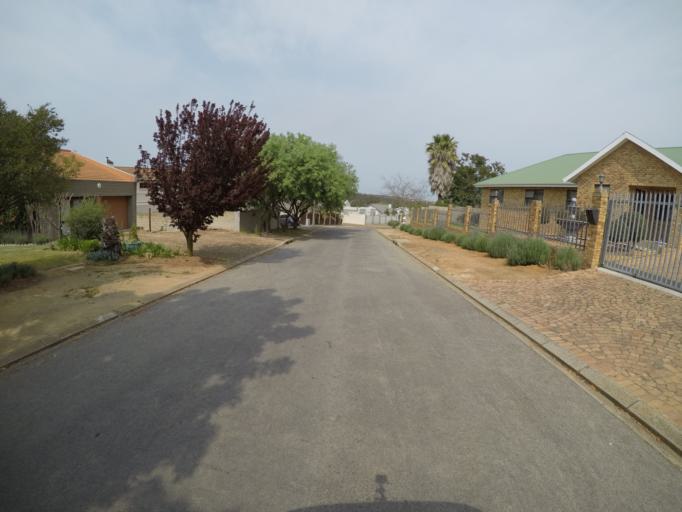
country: ZA
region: Western Cape
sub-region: West Coast District Municipality
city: Malmesbury
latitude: -33.4606
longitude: 18.7415
